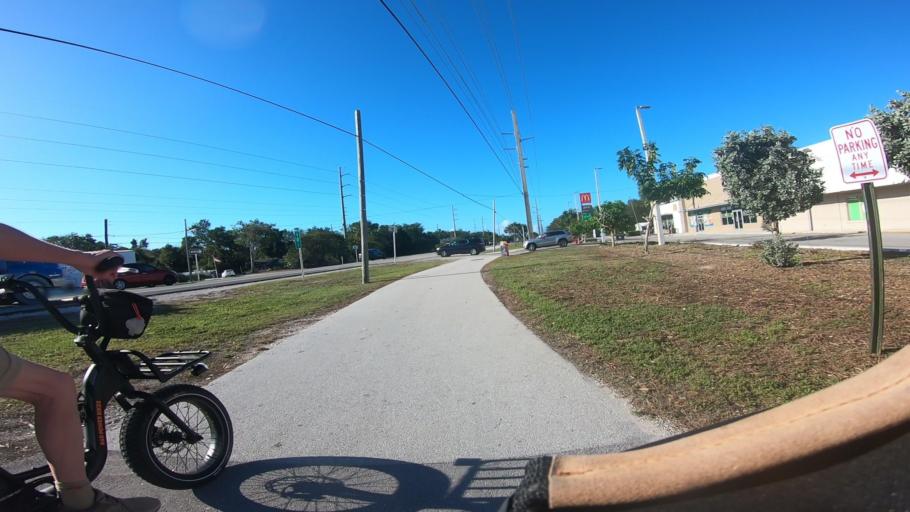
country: US
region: Florida
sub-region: Monroe County
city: Key Largo
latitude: 25.1090
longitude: -80.4268
